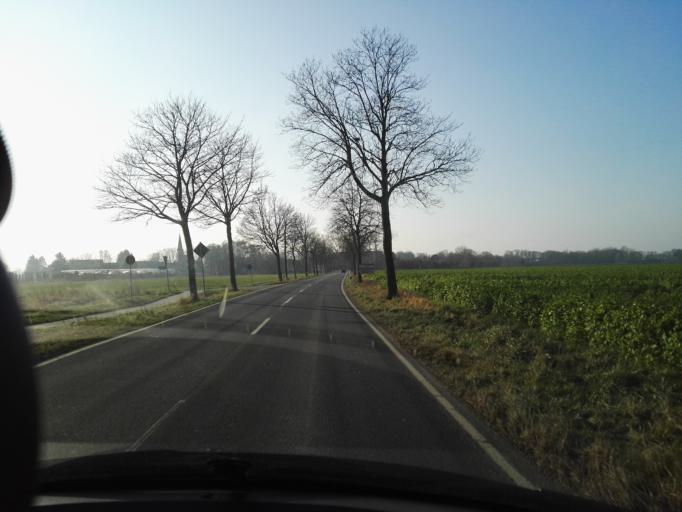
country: DE
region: Lower Saxony
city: Sarstedt
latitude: 52.2506
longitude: 9.8387
